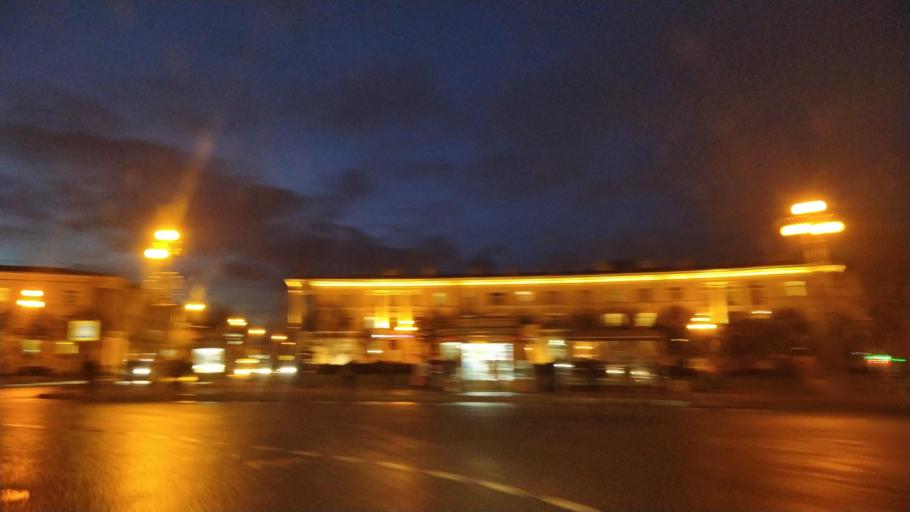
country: RU
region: St.-Petersburg
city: Pushkin
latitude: 59.7231
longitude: 30.4288
